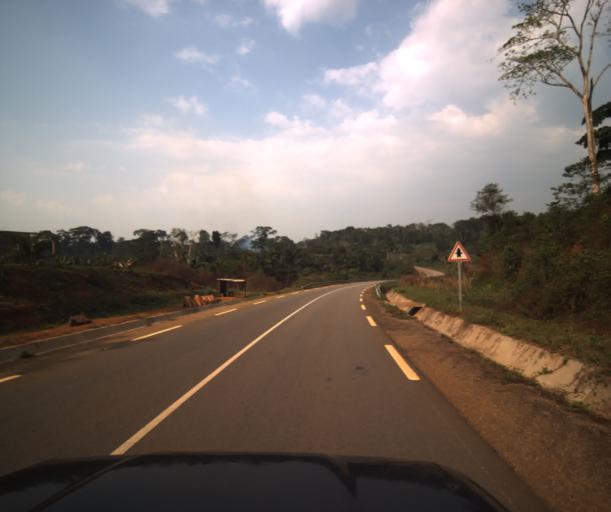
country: CM
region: Centre
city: Mbankomo
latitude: 3.6700
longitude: 11.3464
